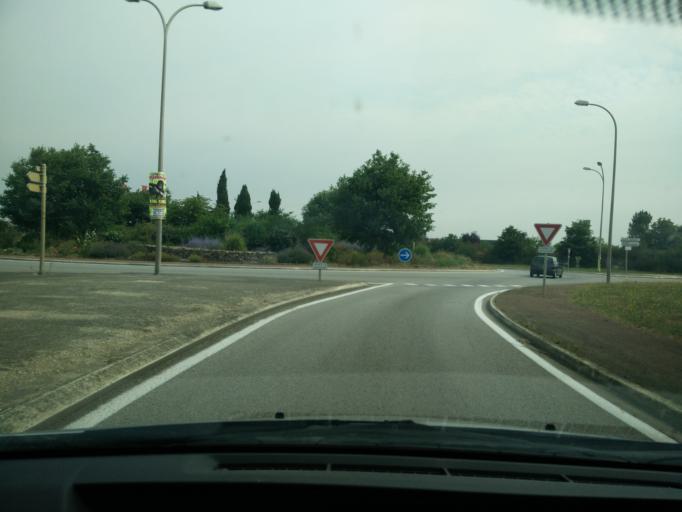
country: FR
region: Poitou-Charentes
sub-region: Departement des Deux-Sevres
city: Thouars
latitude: 46.9896
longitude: -0.1966
